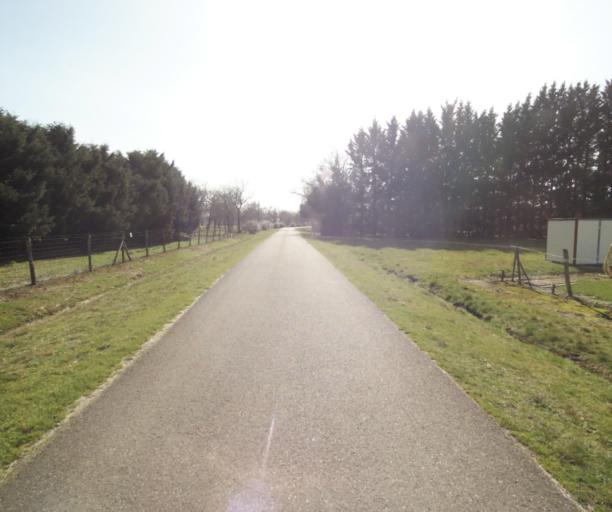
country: FR
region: Aquitaine
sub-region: Departement des Landes
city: Roquefort
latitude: 44.1539
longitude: -0.2507
